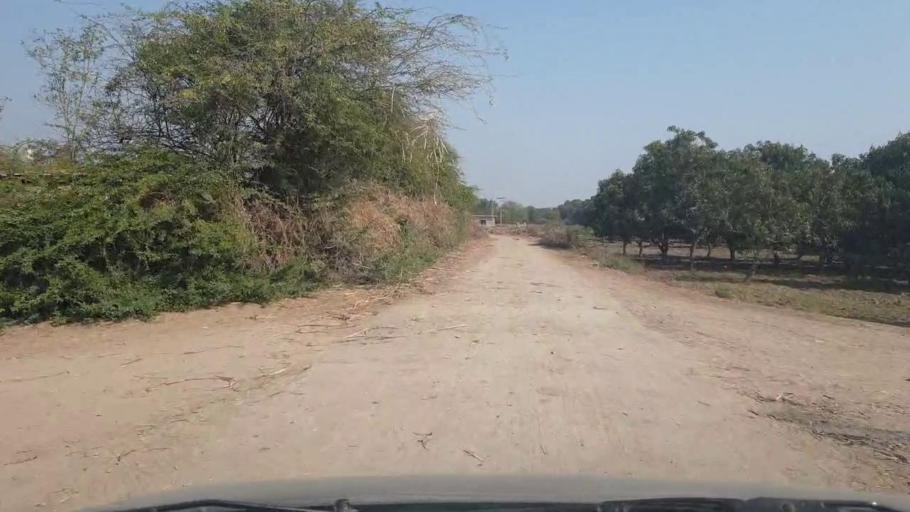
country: PK
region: Sindh
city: Mirwah Gorchani
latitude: 25.2578
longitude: 69.0918
